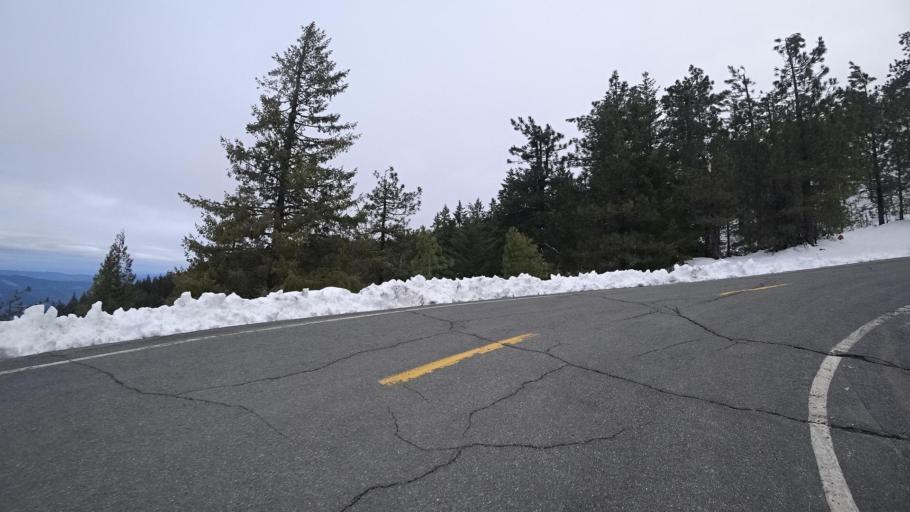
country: US
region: California
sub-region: Humboldt County
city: Willow Creek
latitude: 40.8673
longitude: -123.7378
